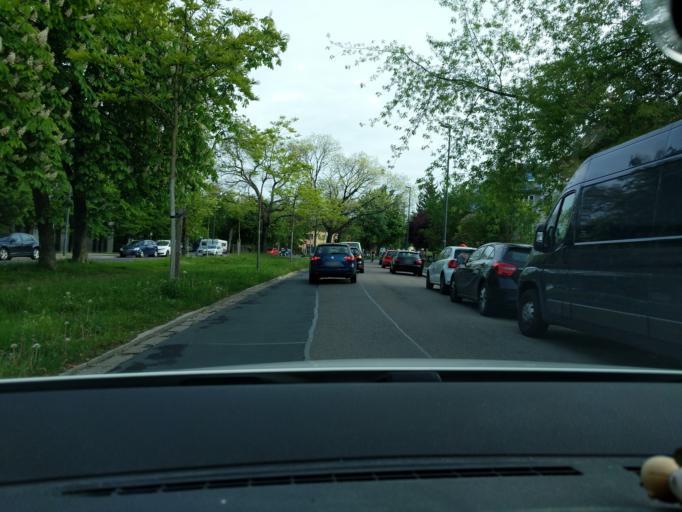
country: DE
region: Saxony
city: Dresden
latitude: 51.0390
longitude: 13.7791
